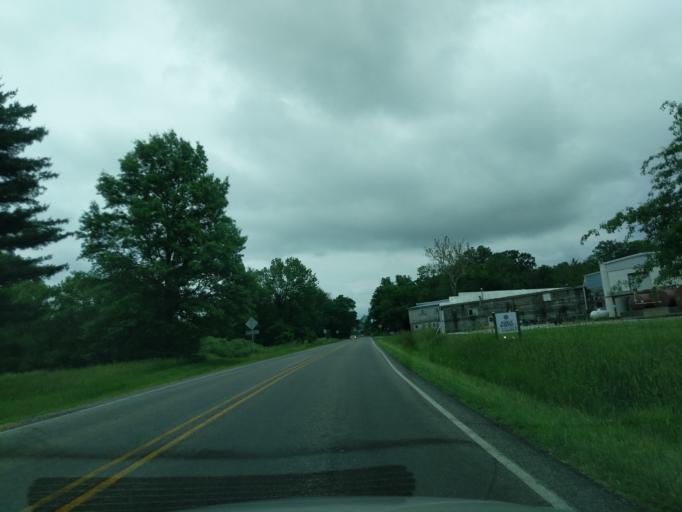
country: US
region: Indiana
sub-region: Tipton County
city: Tipton
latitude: 40.2846
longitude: -85.9439
